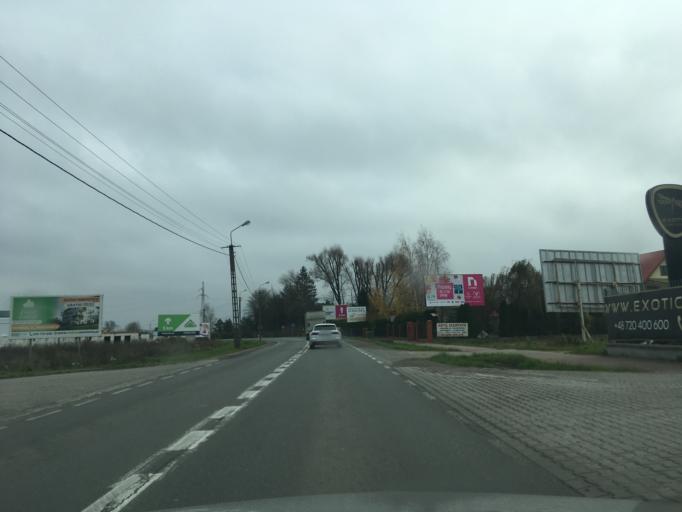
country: PL
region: Masovian Voivodeship
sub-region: Powiat piaseczynski
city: Lesznowola
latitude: 52.0808
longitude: 20.9702
